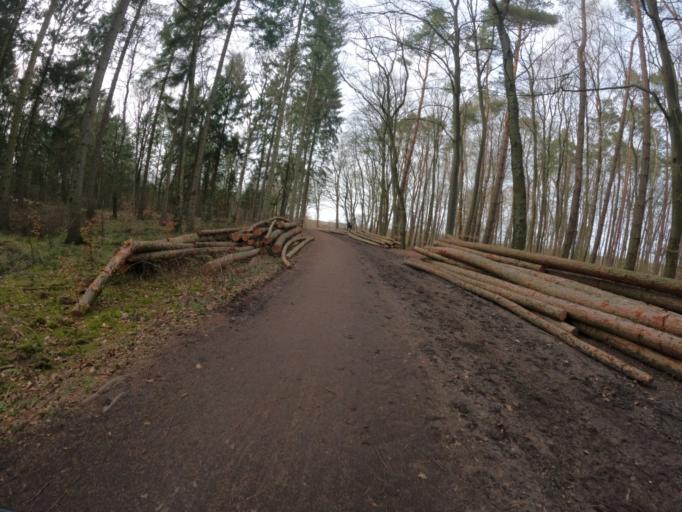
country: DE
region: Schleswig-Holstein
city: Appen
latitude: 53.6087
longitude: 9.7656
